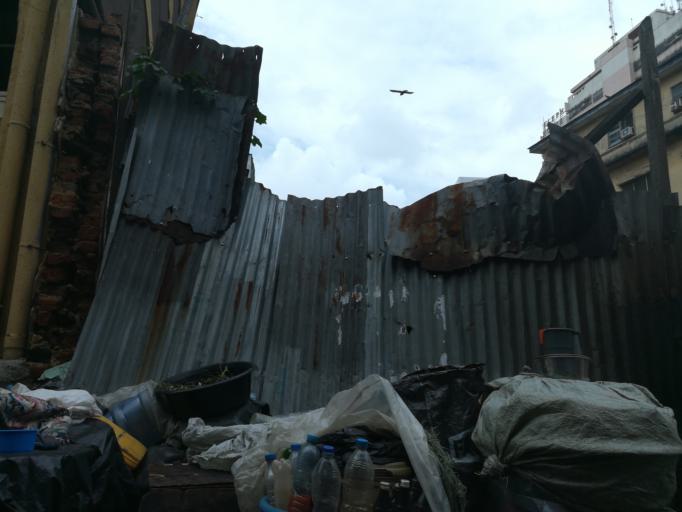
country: NG
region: Lagos
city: Lagos
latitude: 6.4581
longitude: 3.3817
